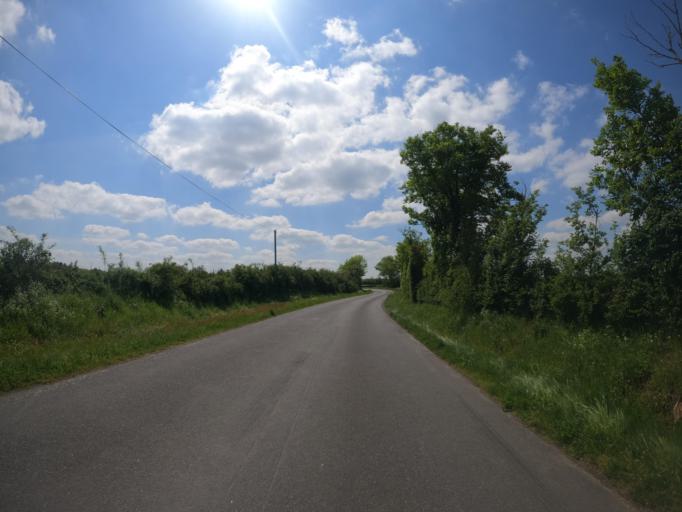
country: FR
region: Poitou-Charentes
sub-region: Departement des Deux-Sevres
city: Saint-Varent
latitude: 46.8178
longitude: -0.2745
